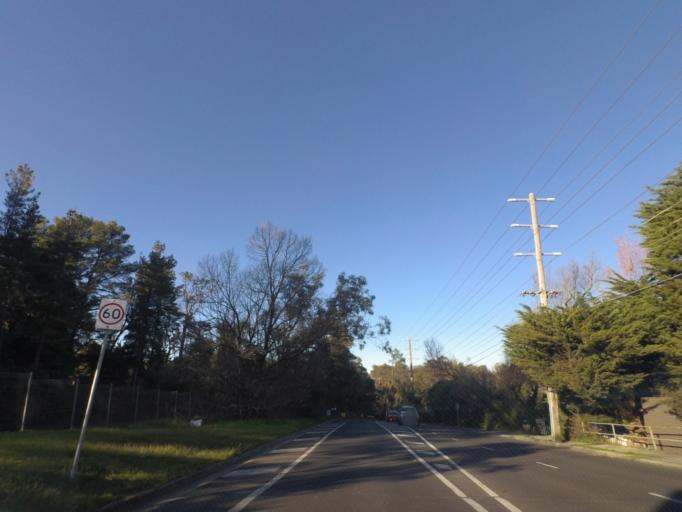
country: AU
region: Victoria
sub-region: Maroondah
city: Croydon South
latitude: -37.8096
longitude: 145.2586
